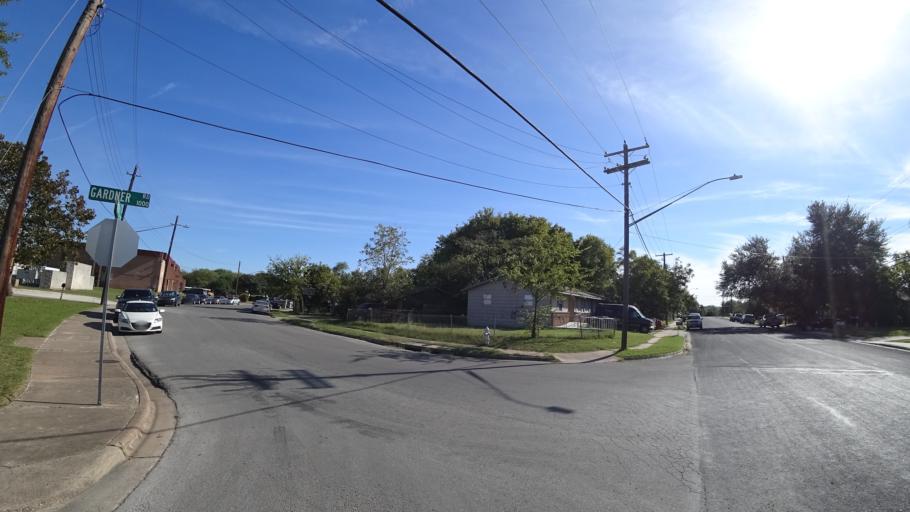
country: US
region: Texas
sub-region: Travis County
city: Austin
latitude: 30.2578
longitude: -97.6830
